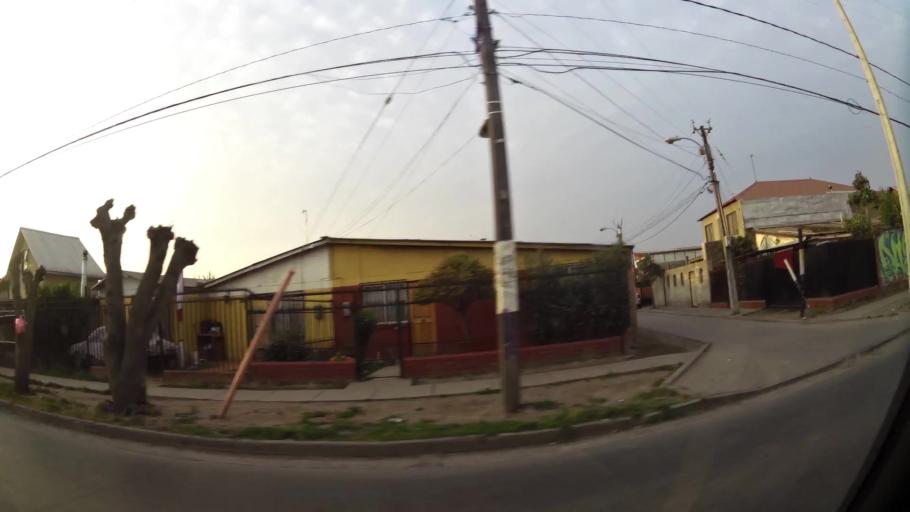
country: CL
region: Santiago Metropolitan
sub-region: Provincia de Santiago
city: Lo Prado
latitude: -33.5158
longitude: -70.7865
